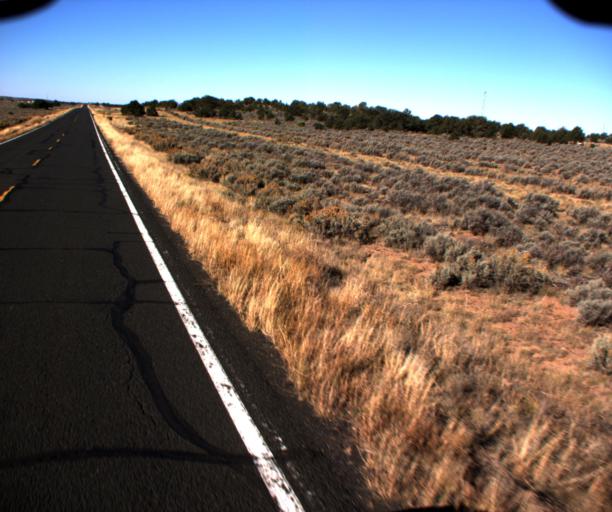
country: US
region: Arizona
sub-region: Navajo County
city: First Mesa
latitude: 35.7397
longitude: -110.0775
